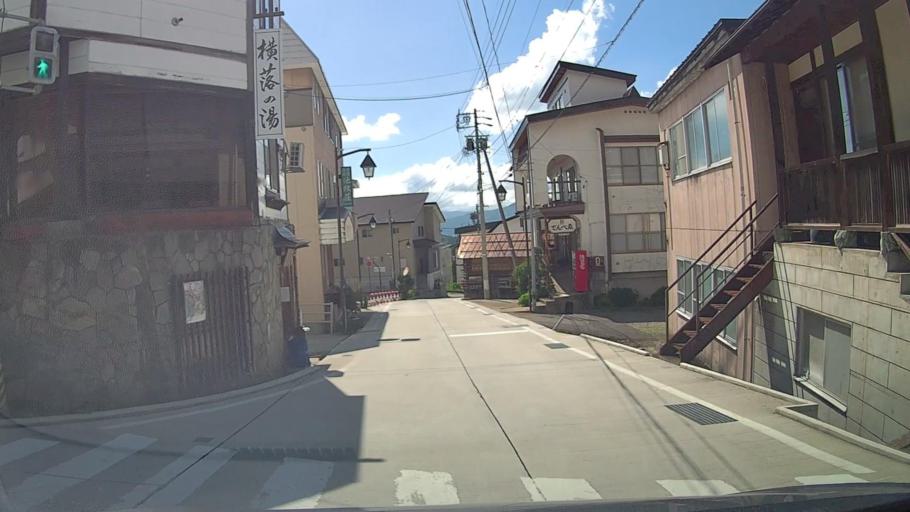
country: JP
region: Nagano
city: Iiyama
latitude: 36.9226
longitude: 138.4461
